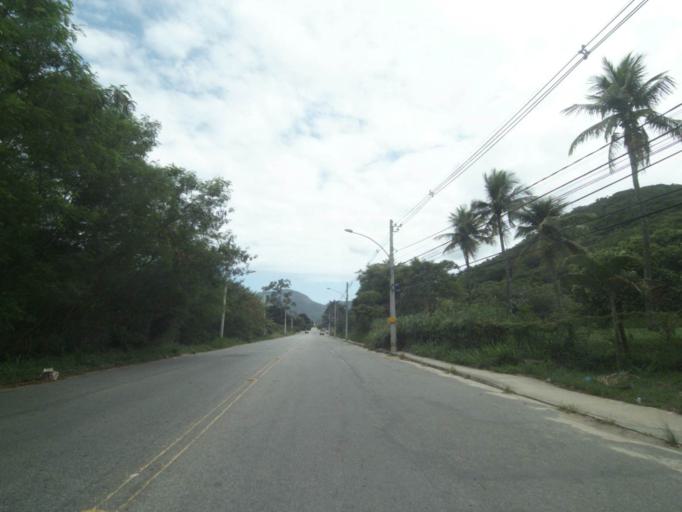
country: BR
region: Rio de Janeiro
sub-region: Nilopolis
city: Nilopolis
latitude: -22.9942
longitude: -43.5077
